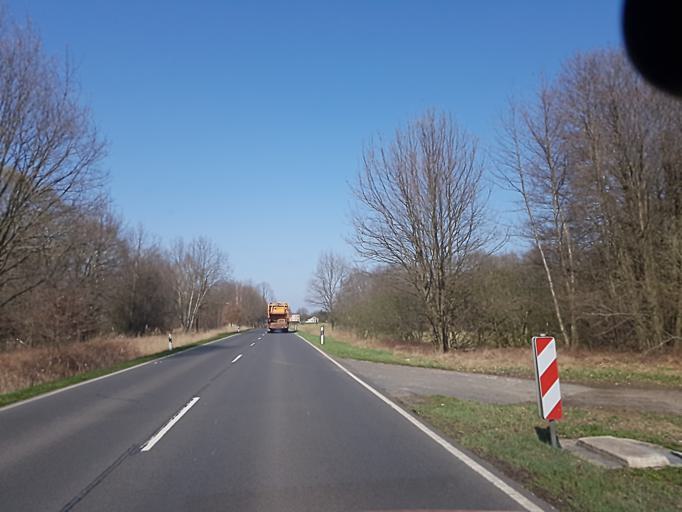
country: DE
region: Brandenburg
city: Forst
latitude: 51.6865
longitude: 14.6006
